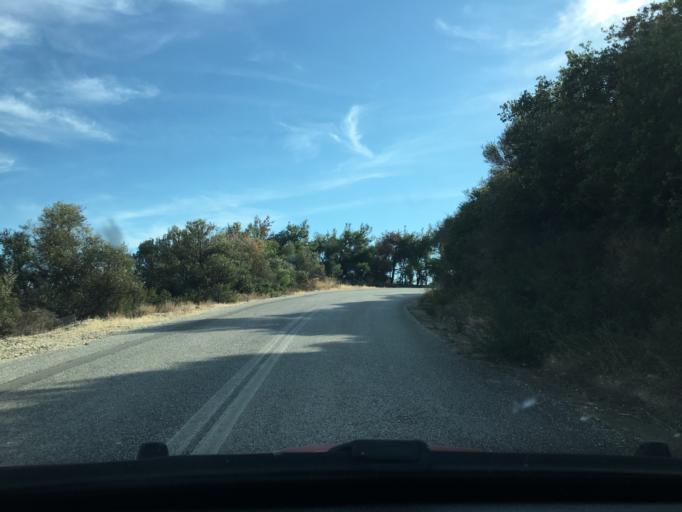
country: GR
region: Central Macedonia
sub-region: Nomos Chalkidikis
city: Agios Nikolaos
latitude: 40.3349
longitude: 23.7138
